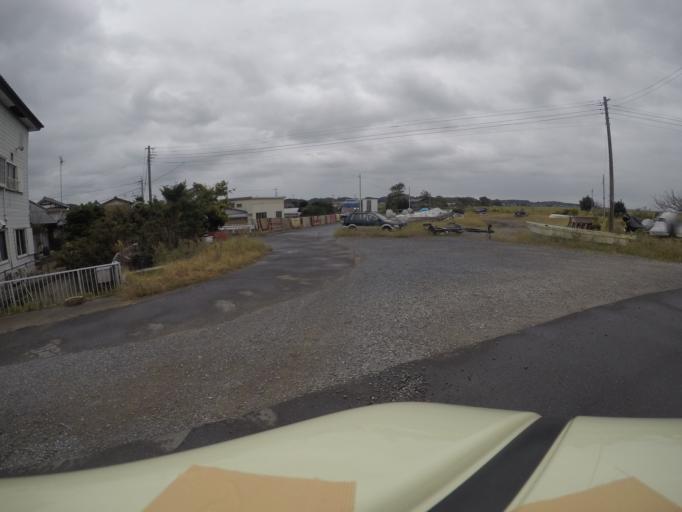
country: JP
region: Ibaraki
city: Itako
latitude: 36.0300
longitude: 140.4540
